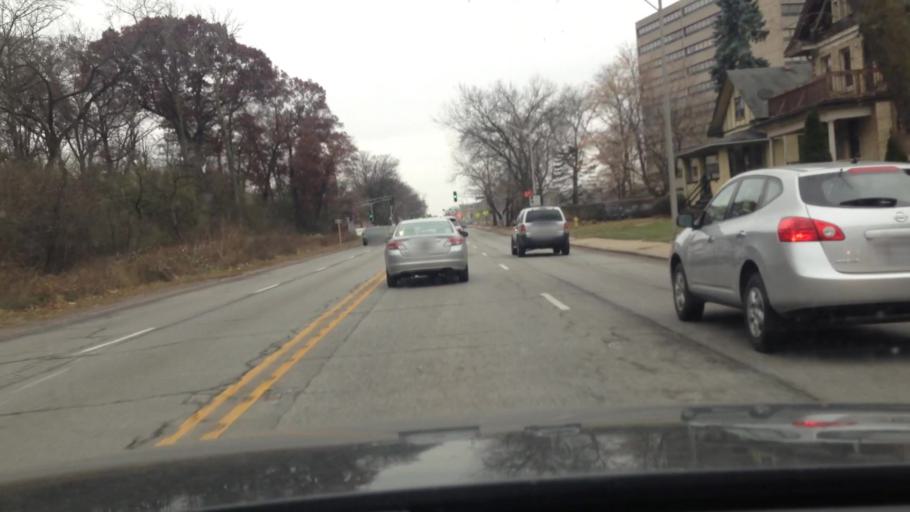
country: US
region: Illinois
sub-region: Cook County
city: Maywood
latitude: 41.8843
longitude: -87.8342
